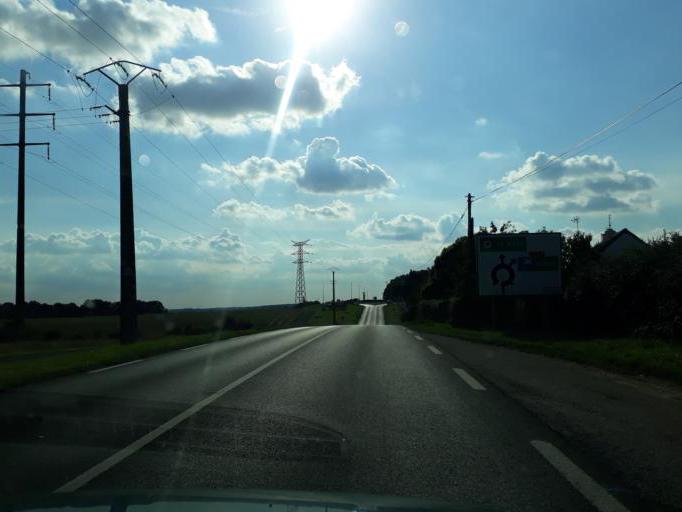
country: FR
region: Centre
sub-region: Departement du Loir-et-Cher
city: Moree
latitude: 47.9042
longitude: 1.2529
